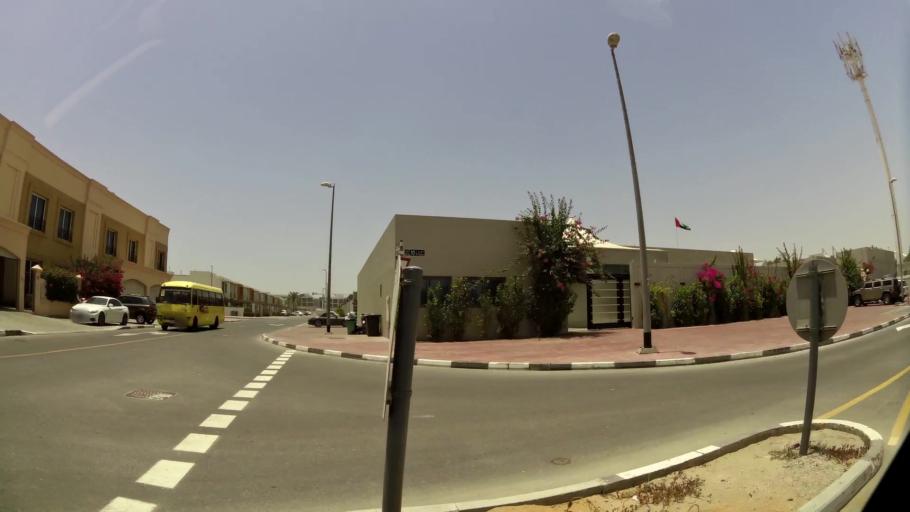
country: AE
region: Dubai
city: Dubai
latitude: 25.1835
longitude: 55.2419
